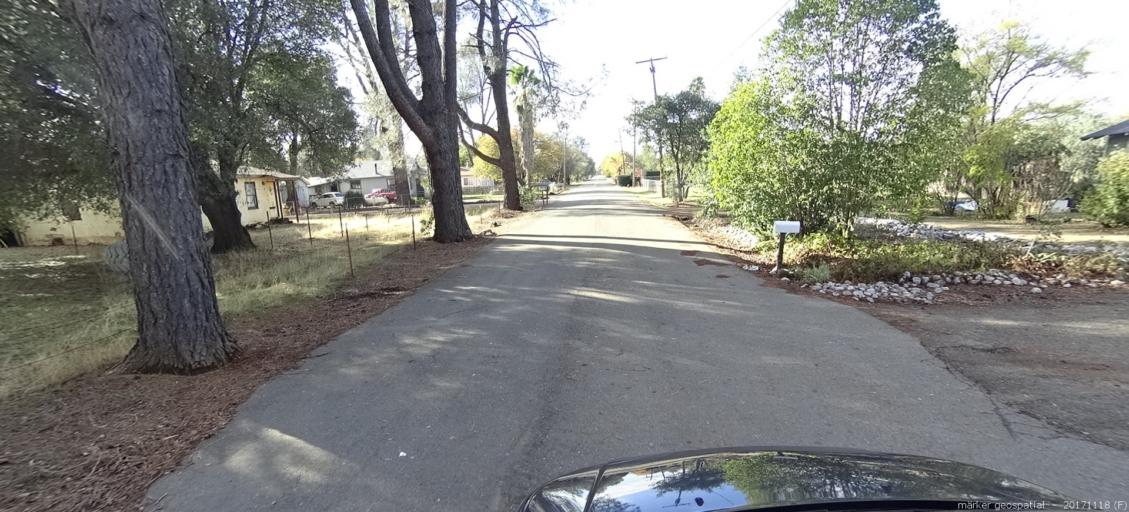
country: US
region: California
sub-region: Shasta County
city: Anderson
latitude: 40.4762
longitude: -122.3879
